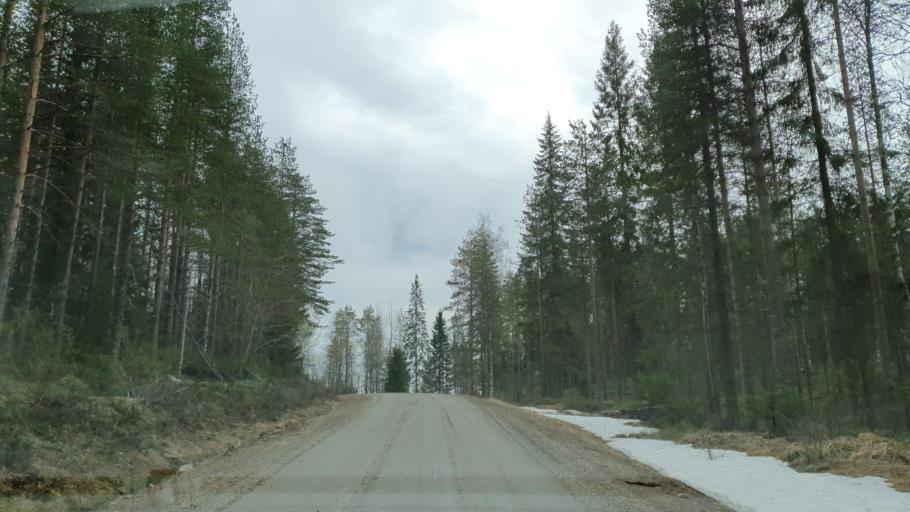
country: FI
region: Kainuu
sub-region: Kehys-Kainuu
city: Kuhmo
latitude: 64.1402
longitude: 29.9661
